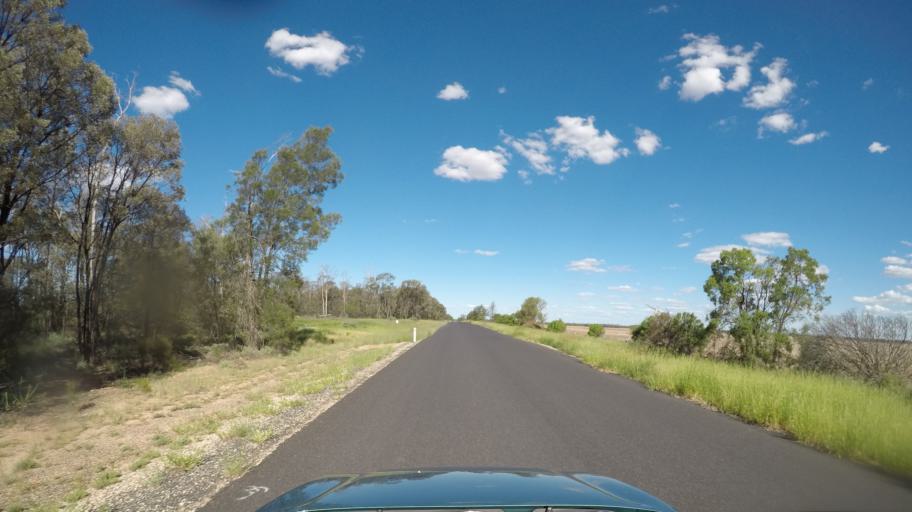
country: AU
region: Queensland
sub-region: Goondiwindi
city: Goondiwindi
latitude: -28.1634
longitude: 150.4244
